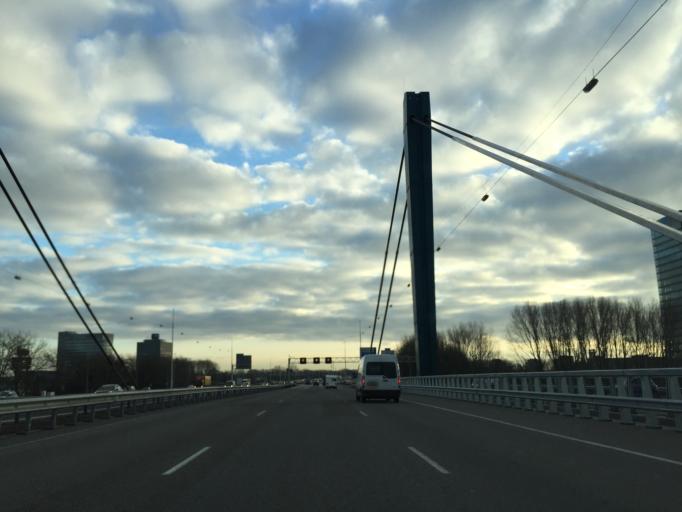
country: NL
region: Utrecht
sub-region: Gemeente Nieuwegein
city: Nieuwegein
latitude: 52.0606
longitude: 5.0979
